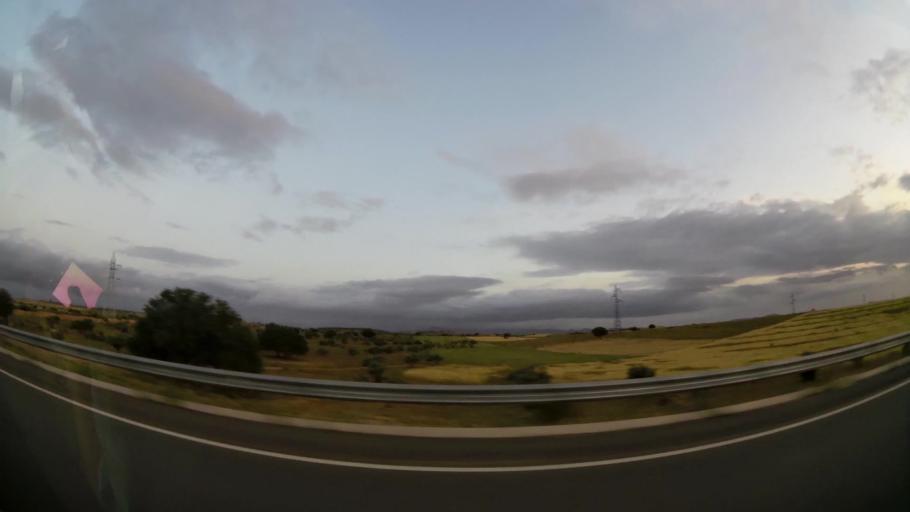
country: MA
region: Oriental
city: El Aioun
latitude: 34.6254
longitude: -2.5086
